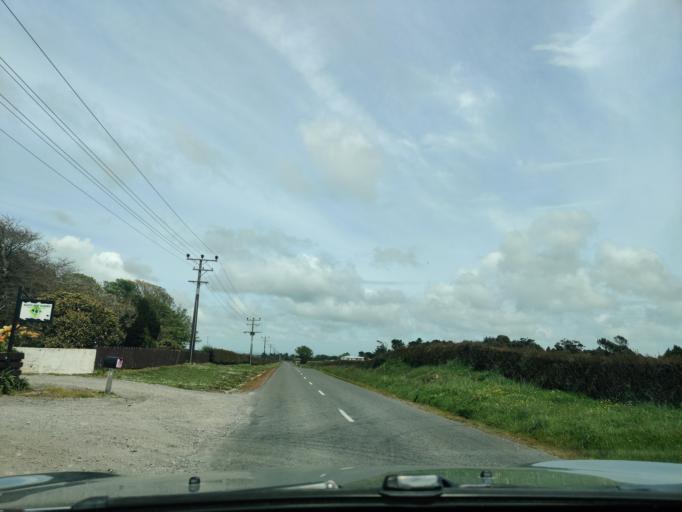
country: NZ
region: Taranaki
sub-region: South Taranaki District
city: Eltham
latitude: -39.3871
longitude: 174.1454
